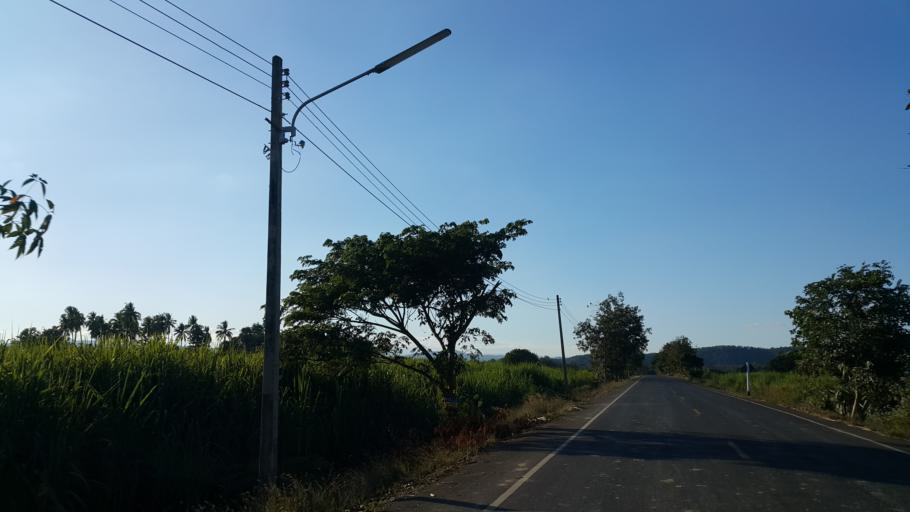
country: TH
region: Sukhothai
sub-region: Amphoe Si Satchanalai
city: Si Satchanalai
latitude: 17.5403
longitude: 99.7973
